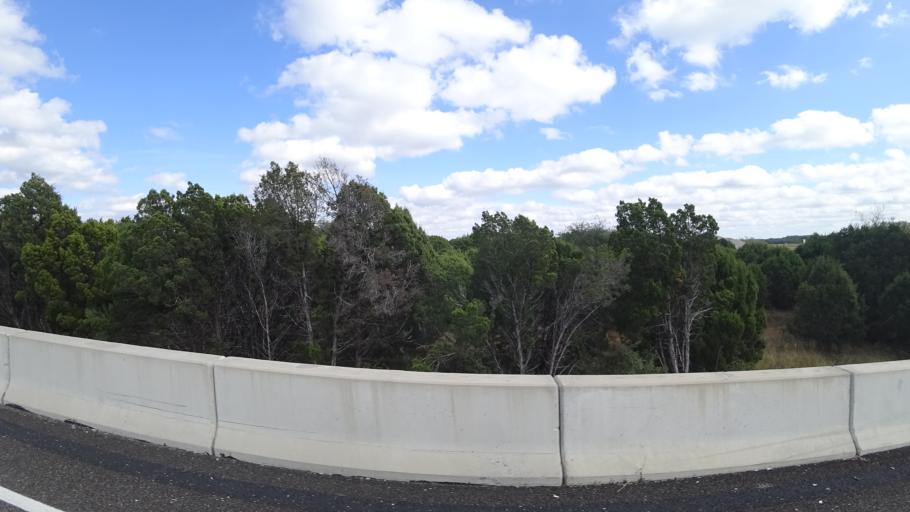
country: US
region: Texas
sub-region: Travis County
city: Bee Cave
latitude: 30.2762
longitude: -97.9145
